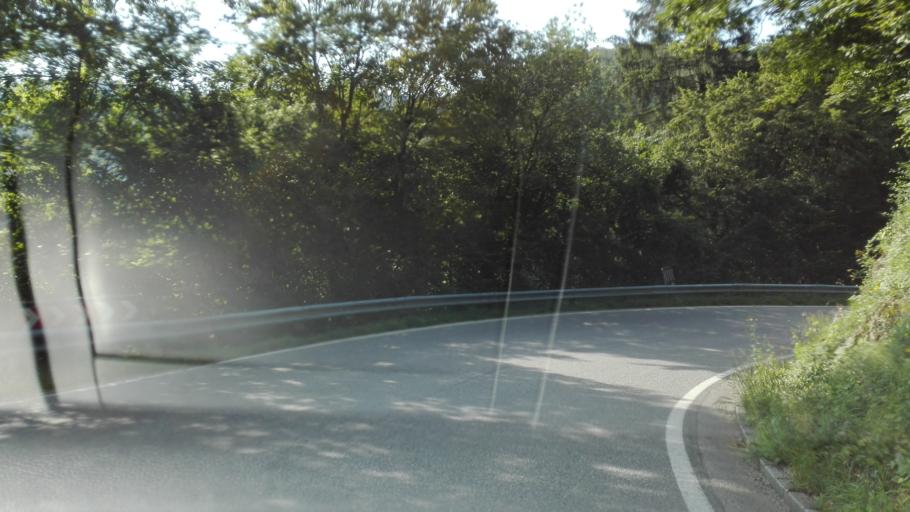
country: AT
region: Lower Austria
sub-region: Politischer Bezirk Sankt Polten
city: Rabenstein an der Pielach
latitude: 48.0349
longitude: 15.4923
